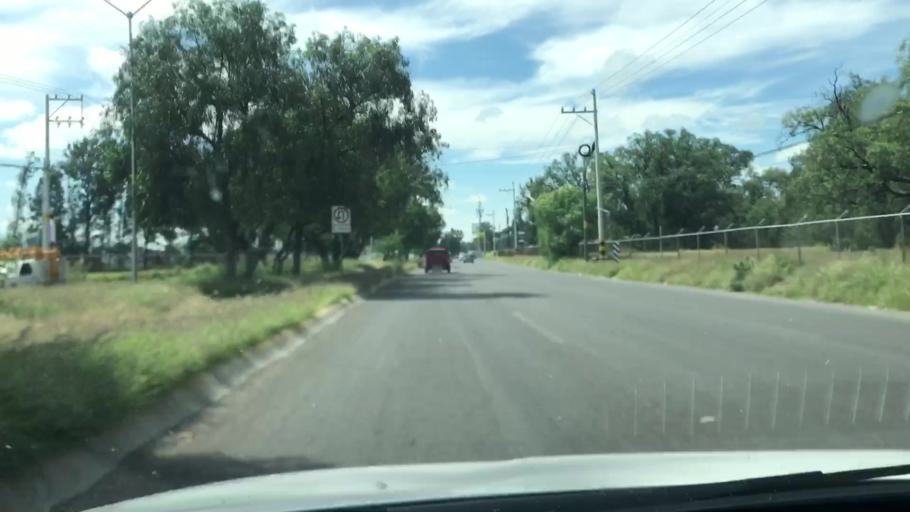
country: MX
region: Guanajuato
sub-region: Celaya
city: La Trinidad
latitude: 20.5291
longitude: -100.7769
